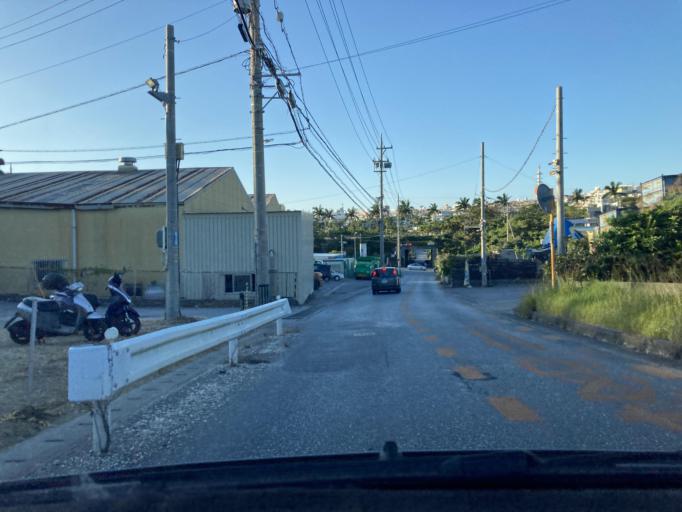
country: JP
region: Okinawa
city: Naha-shi
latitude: 26.2112
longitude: 127.7301
